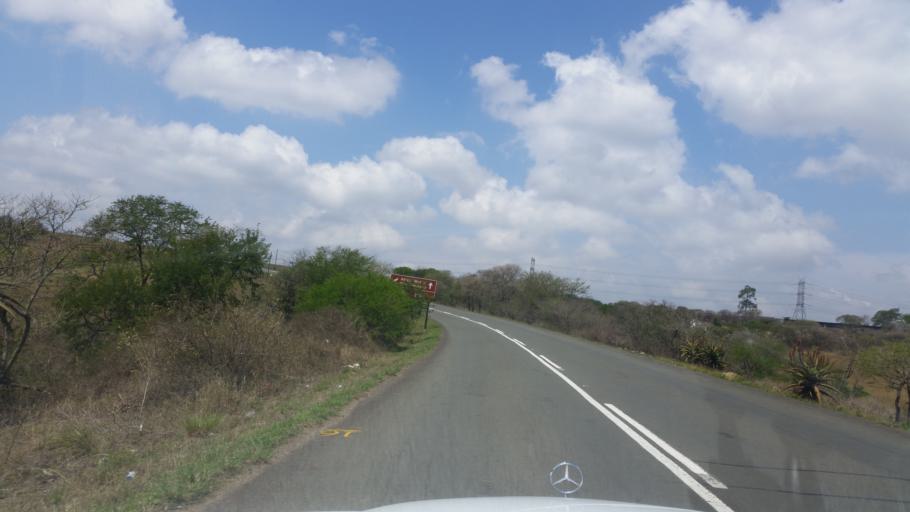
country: ZA
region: KwaZulu-Natal
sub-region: uMgungundlovu District Municipality
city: Camperdown
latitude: -29.6937
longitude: 30.4880
